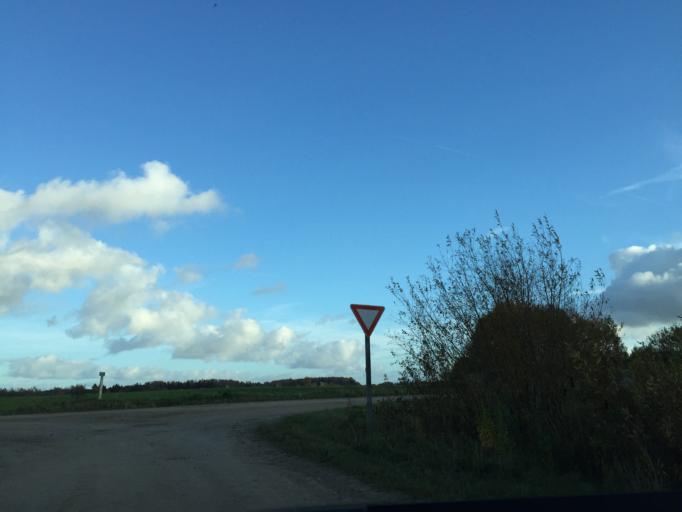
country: LV
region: Ogre
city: Jumprava
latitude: 56.7574
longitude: 25.0170
